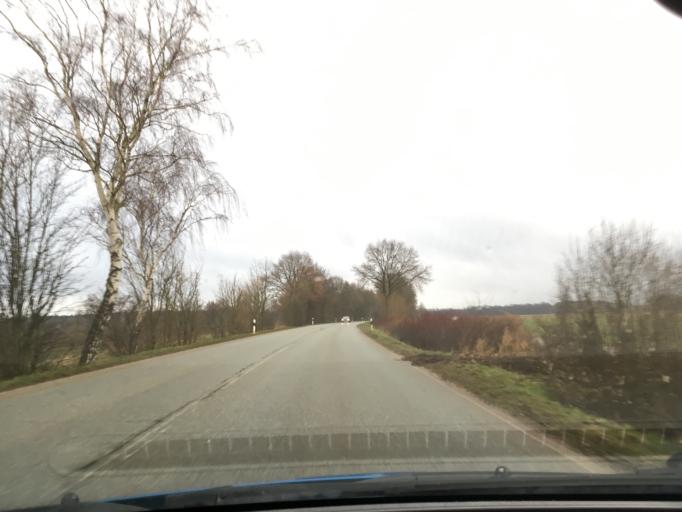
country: DE
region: Schleswig-Holstein
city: Siebeneichen
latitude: 53.5141
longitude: 10.6133
